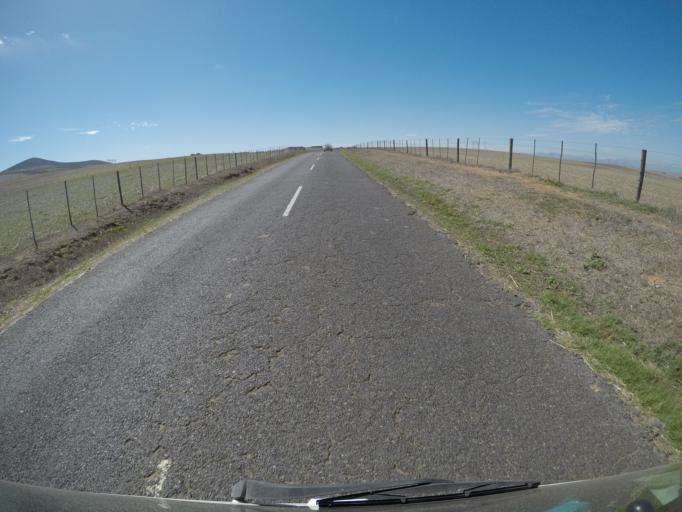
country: ZA
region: Western Cape
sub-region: City of Cape Town
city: Sunset Beach
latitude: -33.7393
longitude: 18.5648
